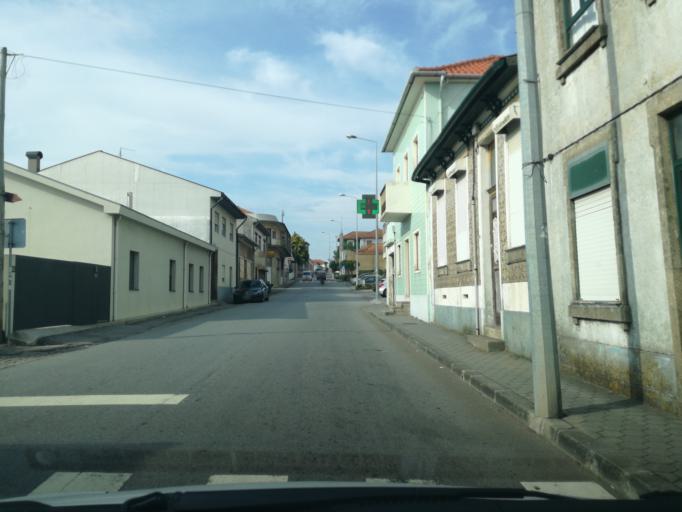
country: PT
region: Porto
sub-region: Vila Nova de Gaia
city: Sao Felix da Marinha
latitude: 41.0492
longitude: -8.6279
